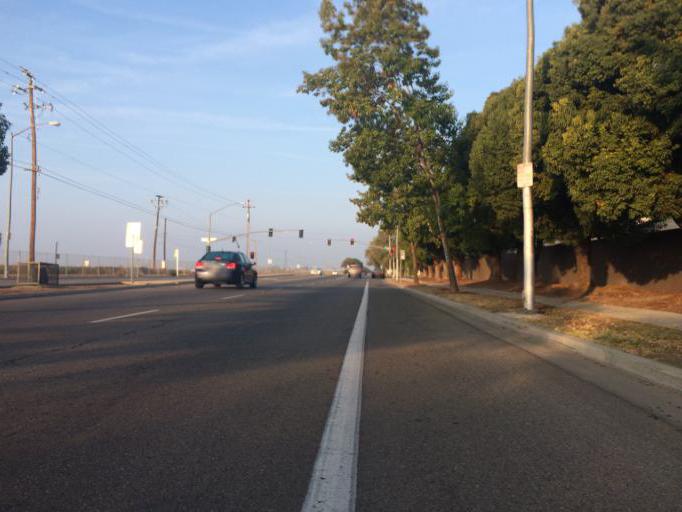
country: US
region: California
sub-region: Fresno County
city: Tarpey Village
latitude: 36.7943
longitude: -119.7351
